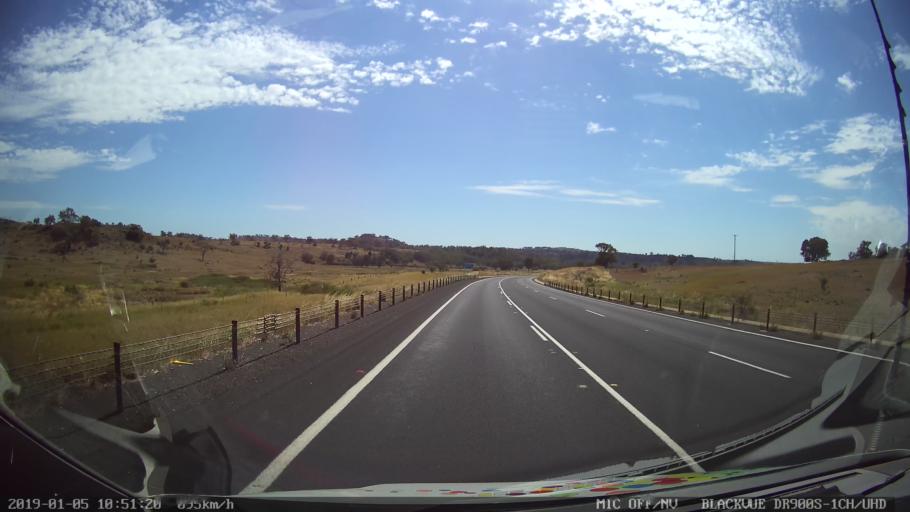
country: AU
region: New South Wales
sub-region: Warrumbungle Shire
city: Coonabarabran
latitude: -31.4254
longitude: 149.0881
